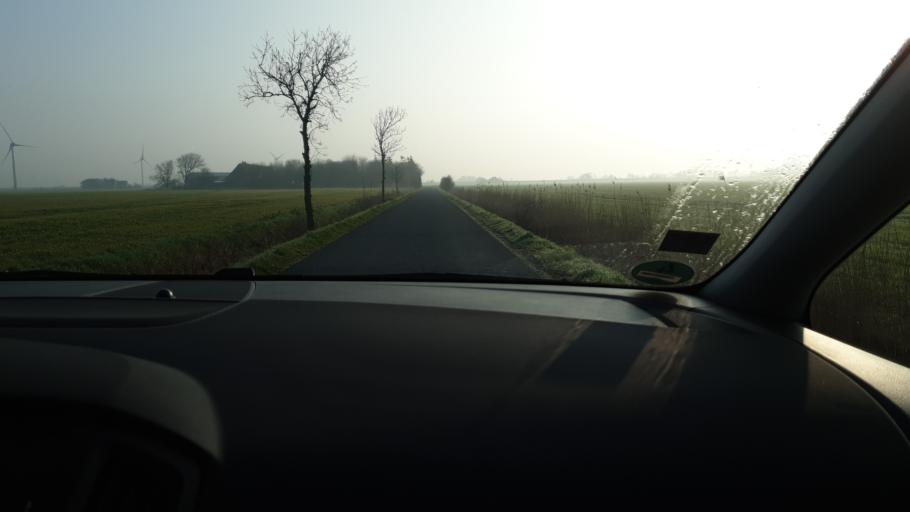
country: DE
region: Schleswig-Holstein
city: Elisabeth-Sophien-Koog
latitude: 54.4981
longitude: 8.8804
